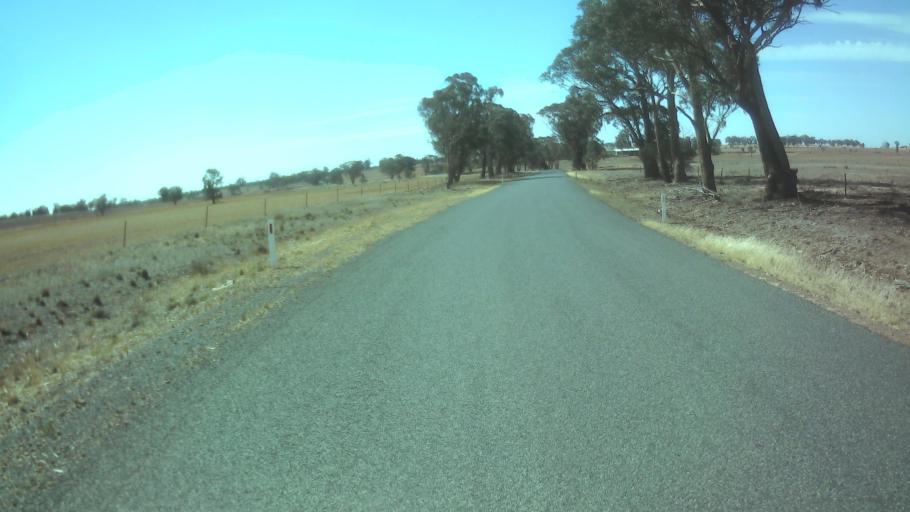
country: AU
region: New South Wales
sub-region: Weddin
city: Grenfell
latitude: -33.7664
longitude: 147.8650
